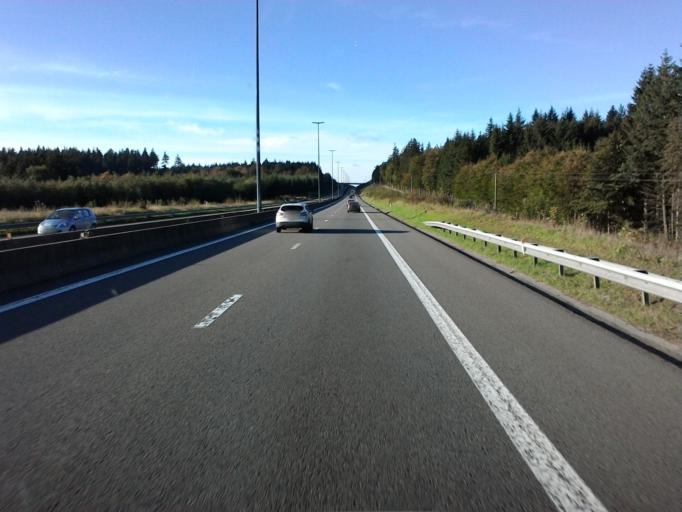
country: BE
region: Wallonia
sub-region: Province du Luxembourg
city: Houffalize
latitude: 50.2084
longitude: 5.7770
